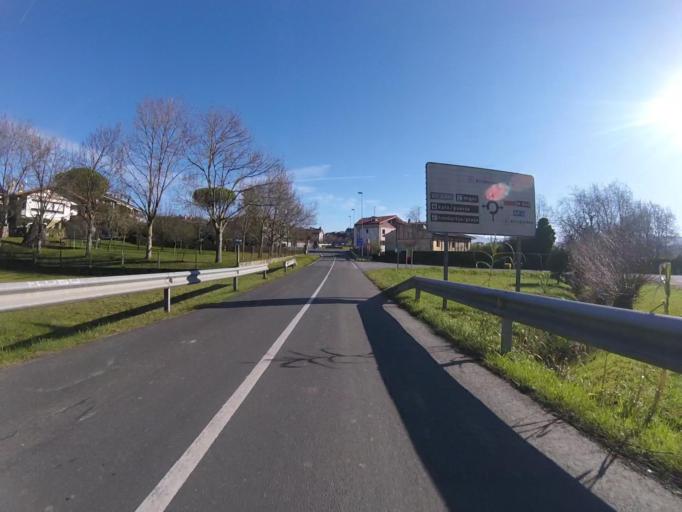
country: ES
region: Basque Country
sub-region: Provincia de Guipuzcoa
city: Fuenterrabia
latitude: 43.3664
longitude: -1.8032
